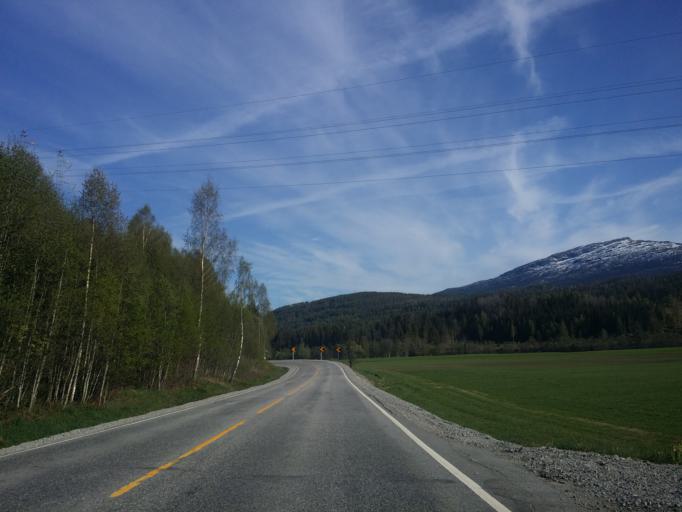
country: NO
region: Telemark
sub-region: Hjartdal
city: Sauland
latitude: 59.6225
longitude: 8.9103
